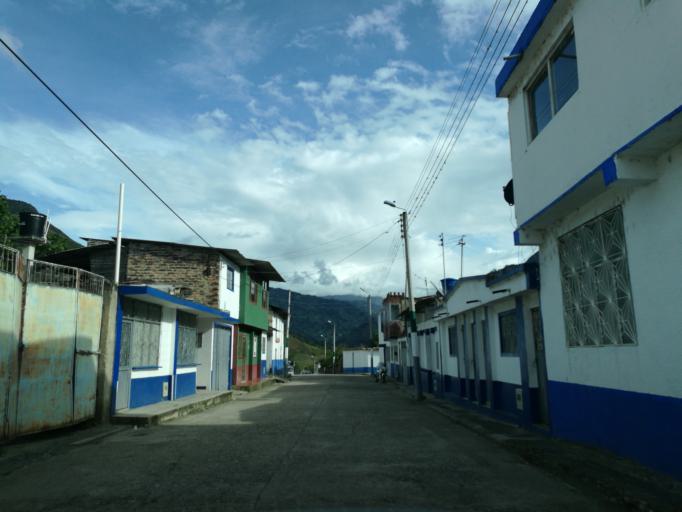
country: CO
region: Boyaca
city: El Espino
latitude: 6.4817
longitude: -72.4967
